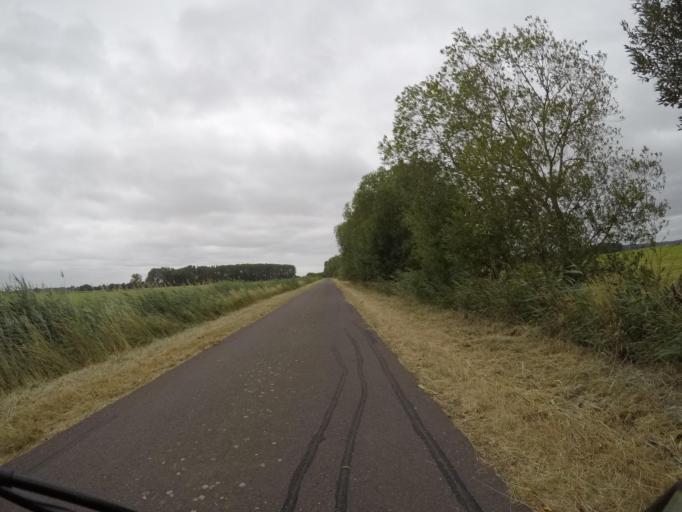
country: DE
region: Lower Saxony
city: Hitzacker
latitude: 53.1635
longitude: 11.0914
